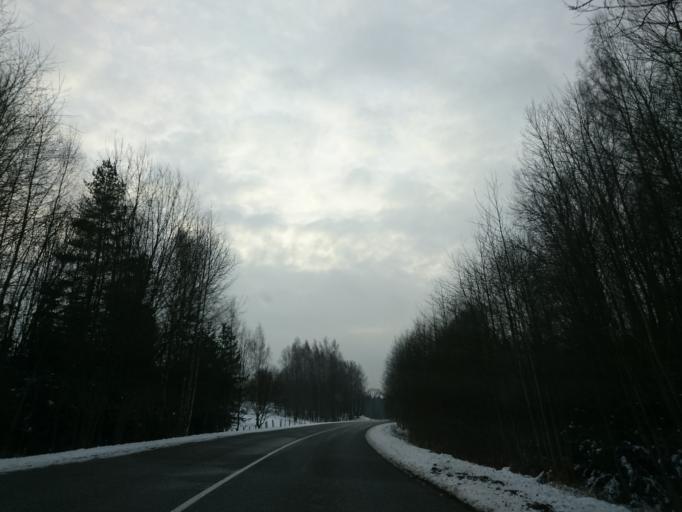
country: LV
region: Seja
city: Loja
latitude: 57.1804
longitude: 24.6065
